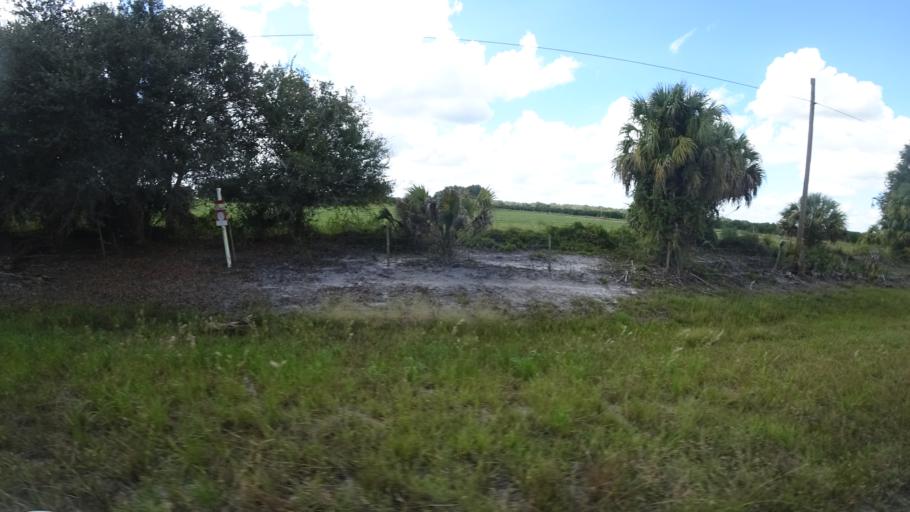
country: US
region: Florida
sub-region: Sarasota County
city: North Port
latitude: 27.2256
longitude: -82.1220
